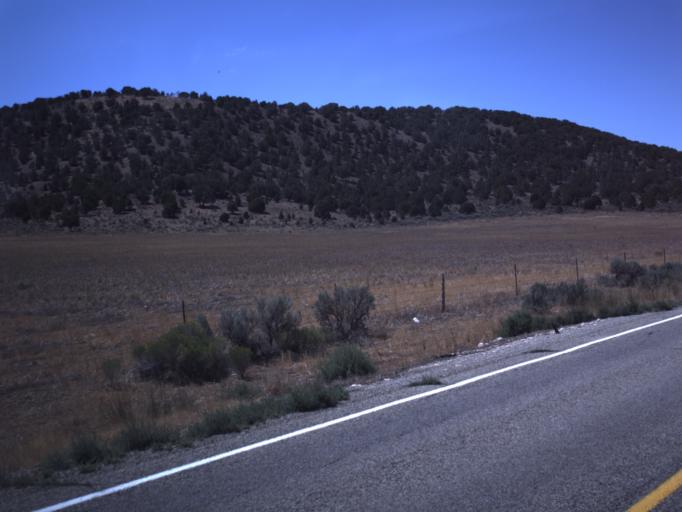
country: US
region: Utah
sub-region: Juab County
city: Nephi
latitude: 39.6971
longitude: -111.9792
